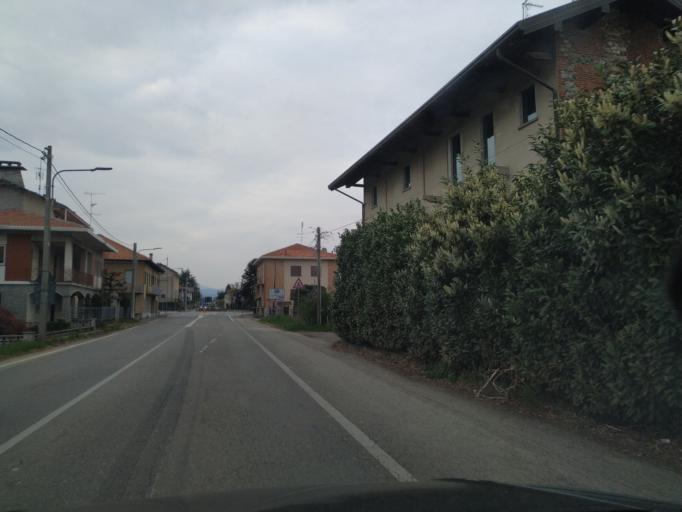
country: IT
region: Piedmont
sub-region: Provincia di Novara
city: Cureggio
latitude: 45.6733
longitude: 8.4558
